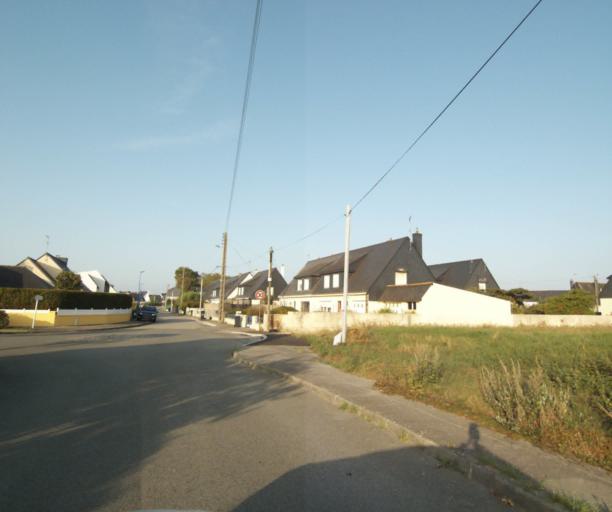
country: FR
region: Brittany
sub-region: Departement du Morbihan
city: Locmiquelic
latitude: 47.7128
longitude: -3.3389
